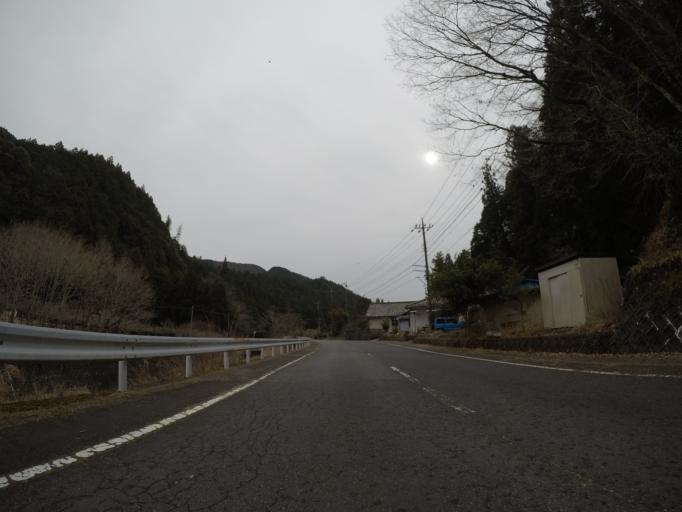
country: JP
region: Shizuoka
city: Fujinomiya
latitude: 35.2728
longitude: 138.5293
